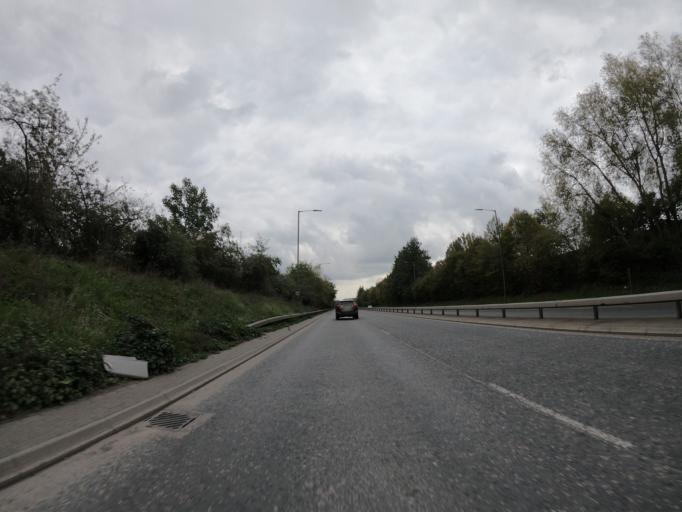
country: GB
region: England
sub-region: Greater London
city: Erith
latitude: 51.4855
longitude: 0.1709
